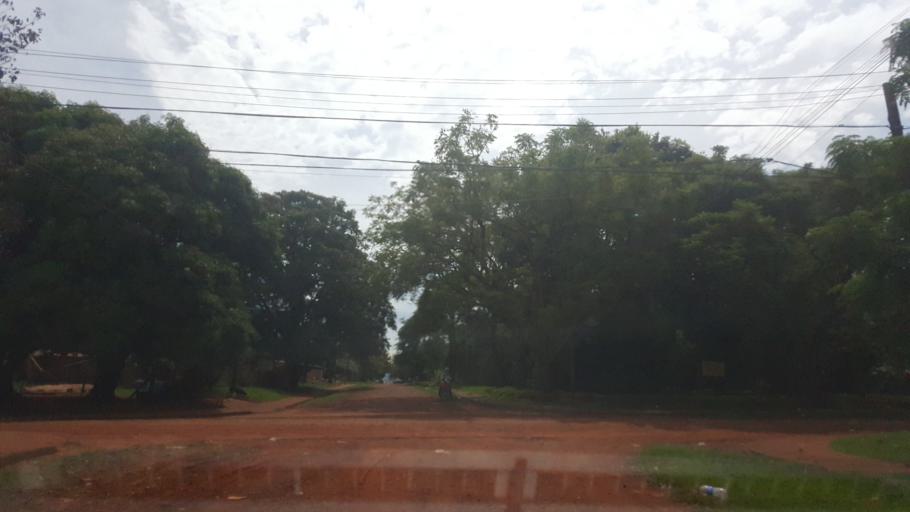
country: AR
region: Misiones
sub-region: Departamento de Capital
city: Posadas
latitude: -27.3984
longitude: -55.9184
